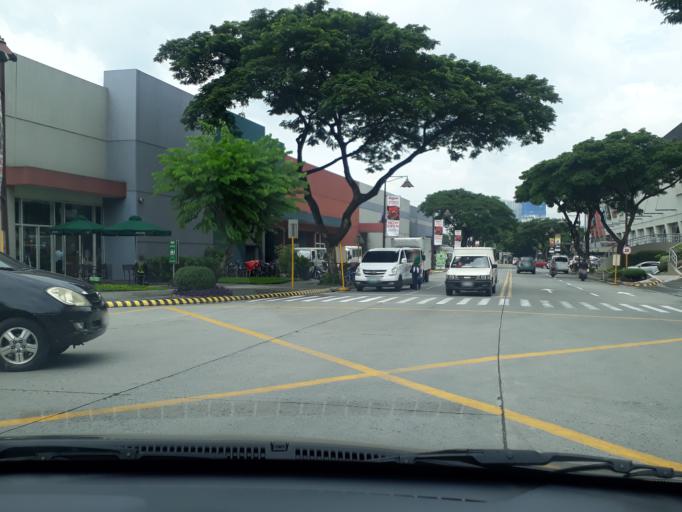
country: PH
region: Metro Manila
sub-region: Pasig
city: Pasig City
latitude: 14.5855
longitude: 121.0770
